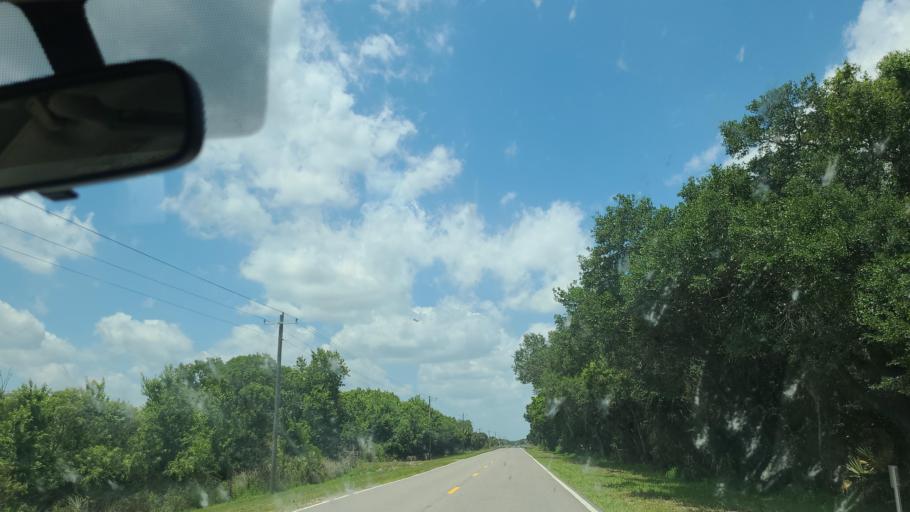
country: US
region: Florida
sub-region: Okeechobee County
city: Cypress Quarters
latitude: 27.3945
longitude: -80.8921
